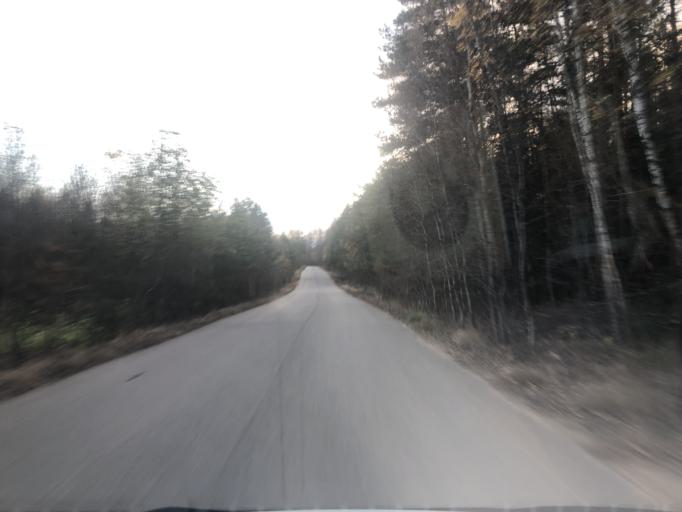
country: RU
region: Moskovskaya
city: Fryanovo
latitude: 56.1562
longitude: 38.3933
